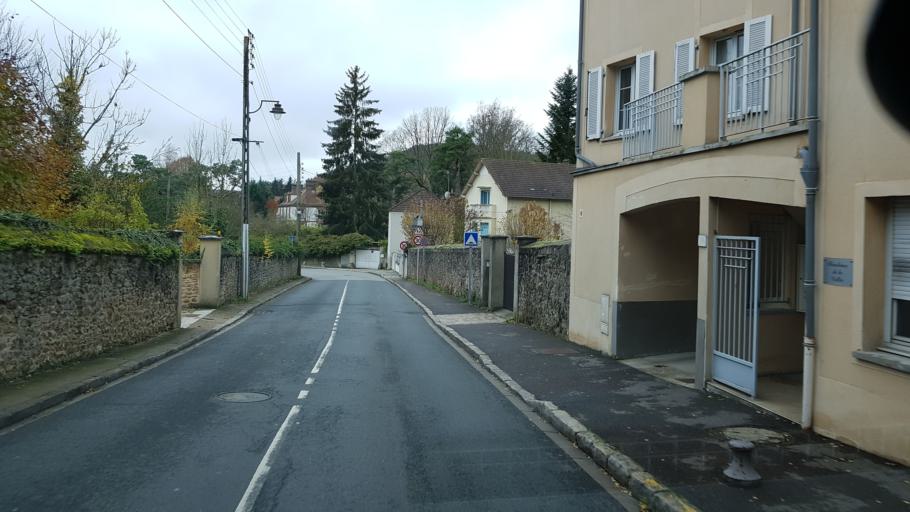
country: FR
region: Ile-de-France
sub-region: Departement des Yvelines
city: Chevreuse
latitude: 48.7093
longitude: 2.0380
